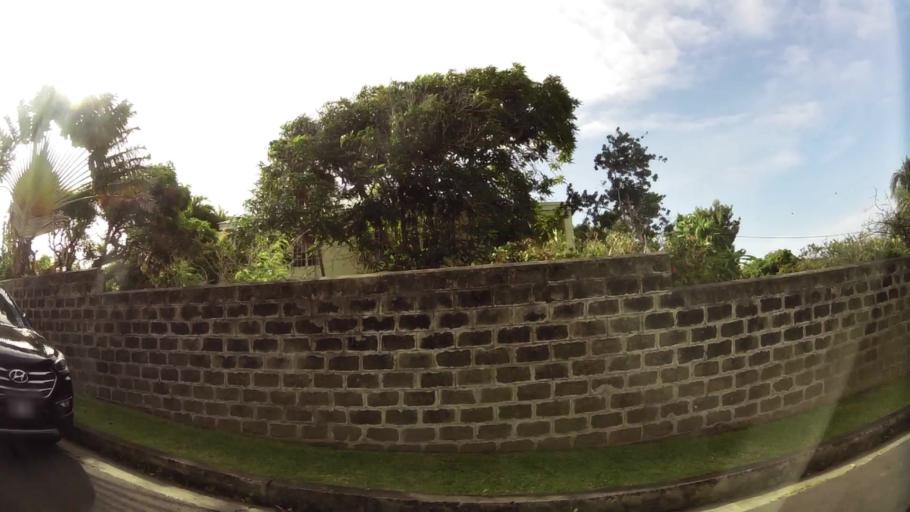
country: KN
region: Saint George Basseterre
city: Basseterre
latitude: 17.2916
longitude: -62.7350
